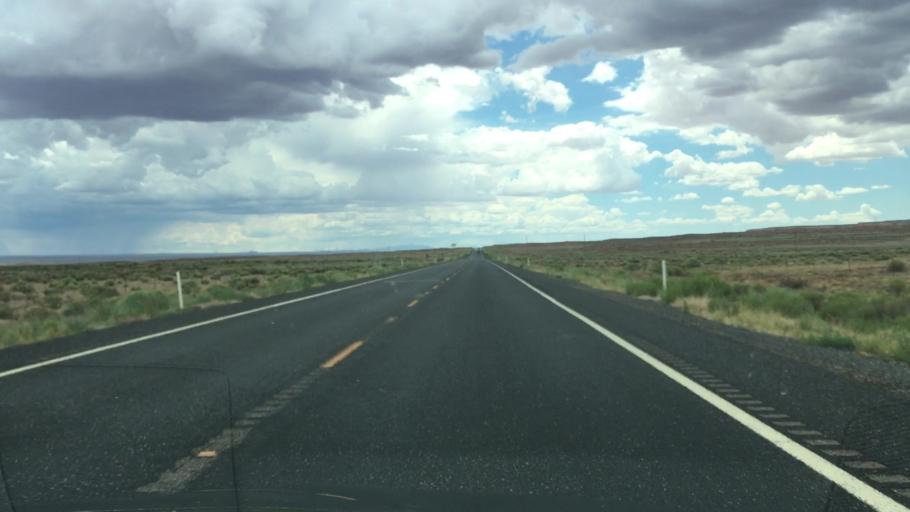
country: US
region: Arizona
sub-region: Coconino County
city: Fredonia
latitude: 36.9270
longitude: -112.5654
